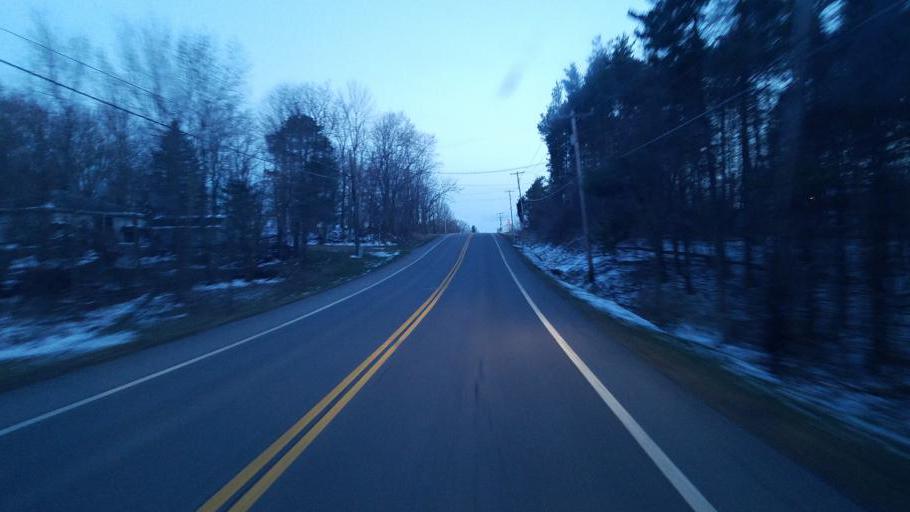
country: US
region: Ohio
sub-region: Ashland County
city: Ashland
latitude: 40.8263
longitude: -82.2822
